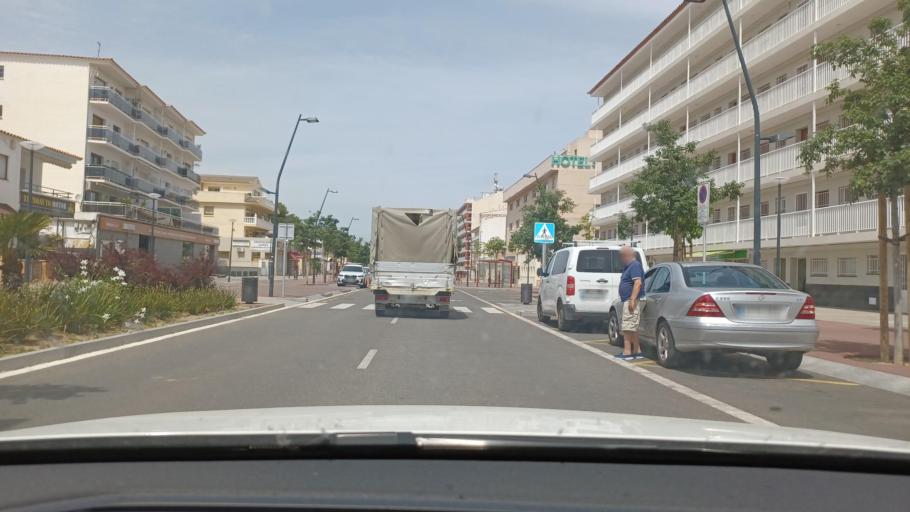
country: ES
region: Catalonia
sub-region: Provincia de Tarragona
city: Colldejou
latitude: 41.0034
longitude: 0.9333
